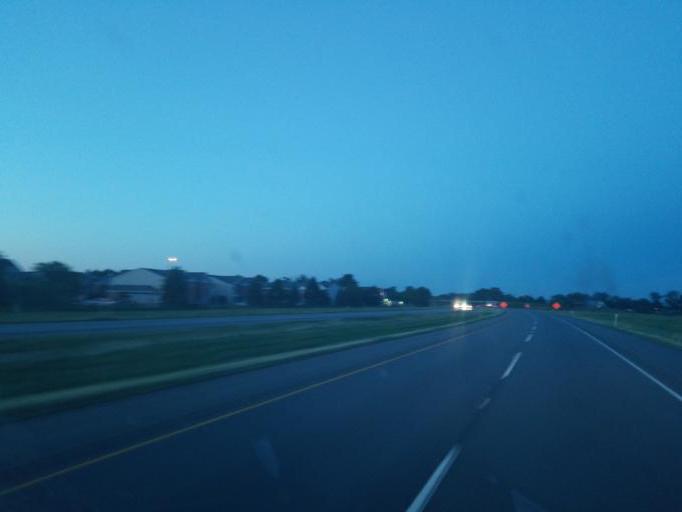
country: US
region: Indiana
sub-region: Saint Joseph County
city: Mishawaka
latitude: 41.7169
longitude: -86.1704
